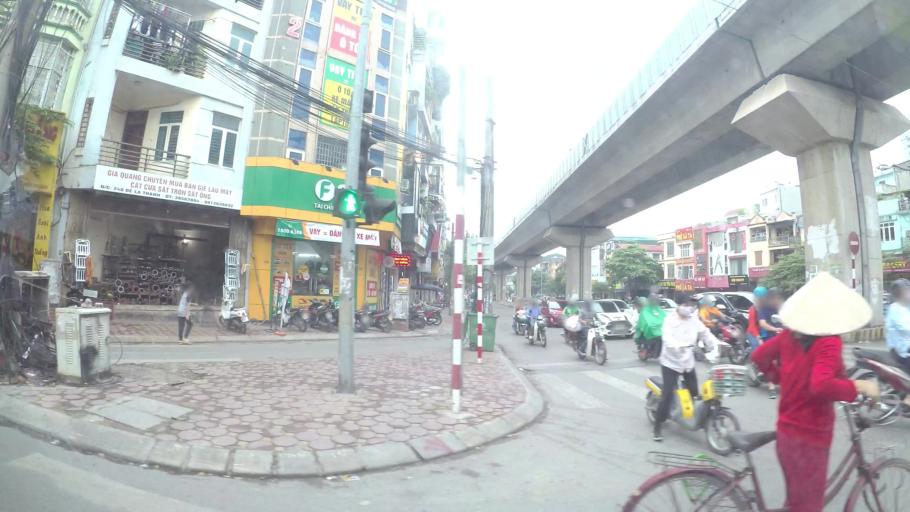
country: VN
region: Ha Noi
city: Dong Da
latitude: 21.0212
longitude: 105.8258
